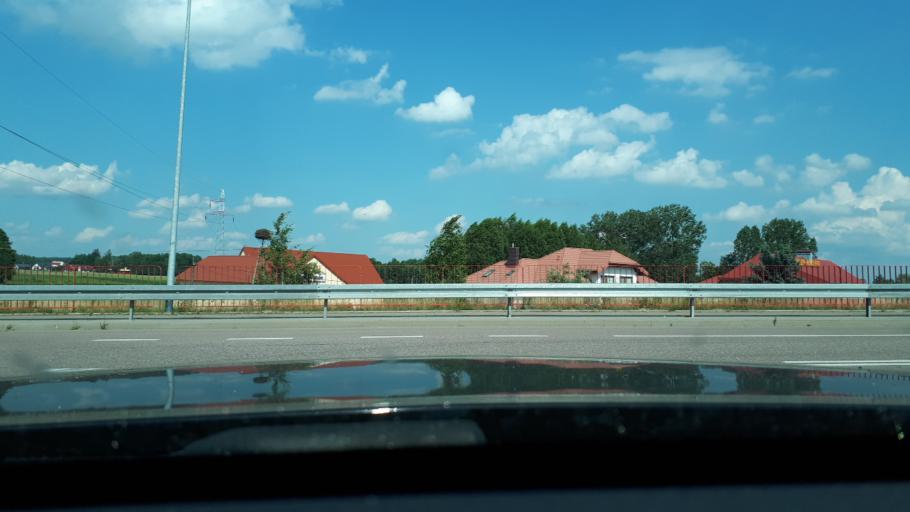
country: PL
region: Podlasie
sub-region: Powiat bialostocki
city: Tykocin
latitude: 53.1567
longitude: 22.8646
